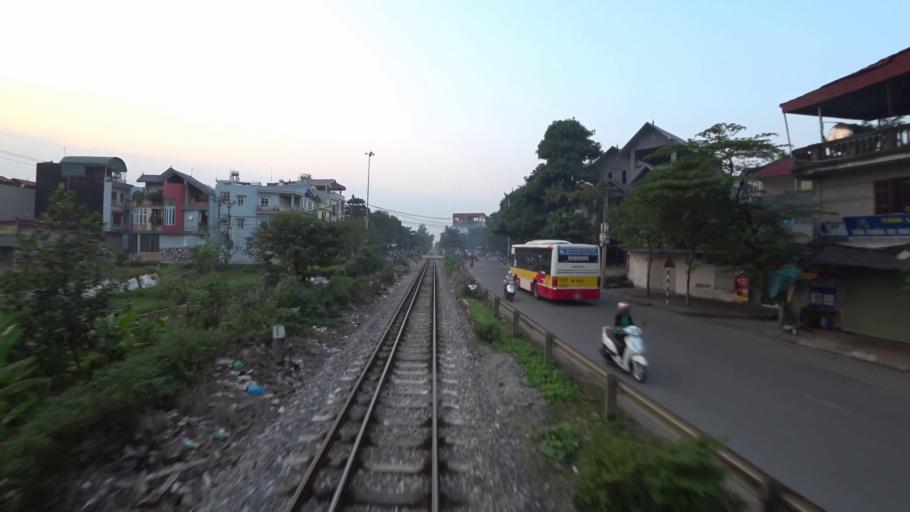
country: VN
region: Ha Noi
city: Dong Anh
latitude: 21.1419
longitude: 105.8645
